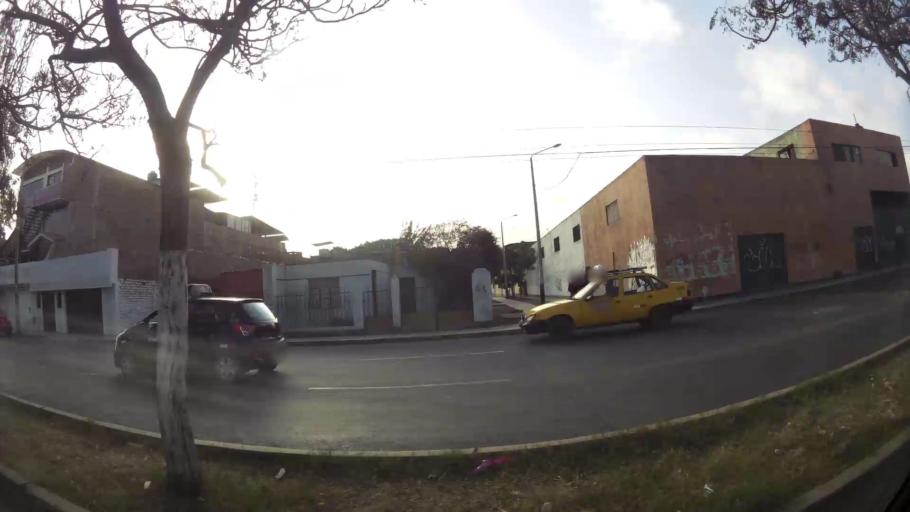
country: PE
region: La Libertad
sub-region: Provincia de Trujillo
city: El Porvenir
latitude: -8.0980
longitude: -79.0126
